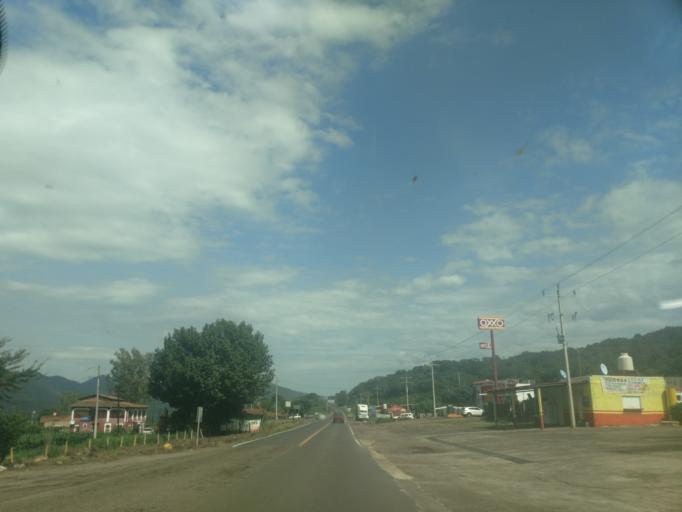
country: MX
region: Jalisco
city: Mascota
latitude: 20.4427
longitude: -104.7529
